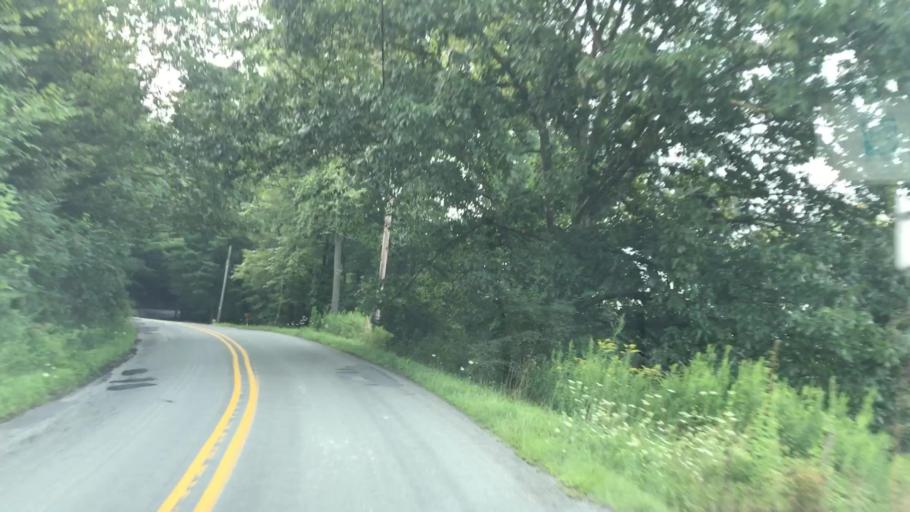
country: US
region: Pennsylvania
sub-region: Wyoming County
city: Factoryville
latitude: 41.6465
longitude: -75.7942
